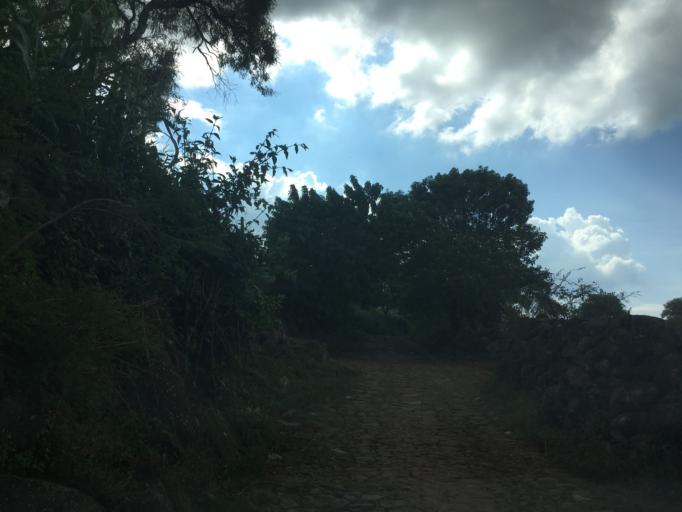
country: MX
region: Mexico
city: El Guayabito
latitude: 19.8982
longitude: -102.5017
